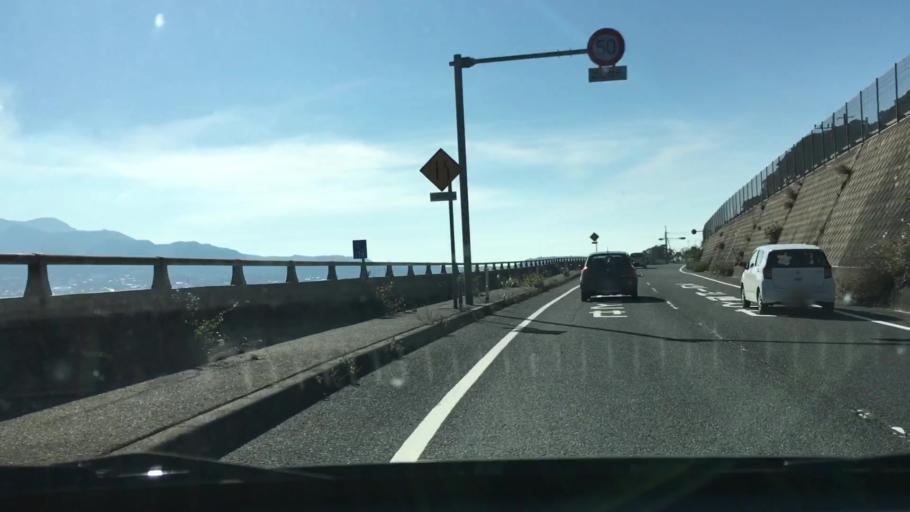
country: JP
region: Kagoshima
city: Kagoshima-shi
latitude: 31.6385
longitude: 130.6027
